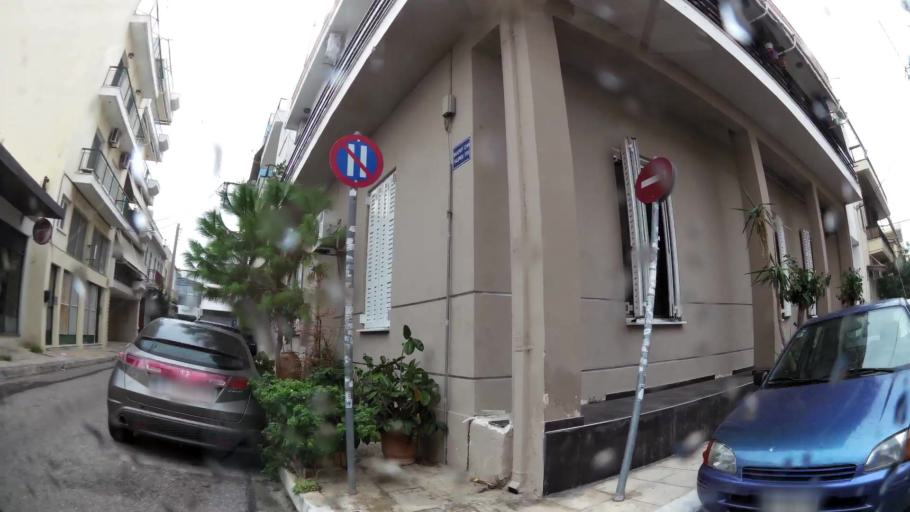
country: GR
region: Attica
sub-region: Nomos Piraios
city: Nikaia
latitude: 37.9608
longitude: 23.6550
